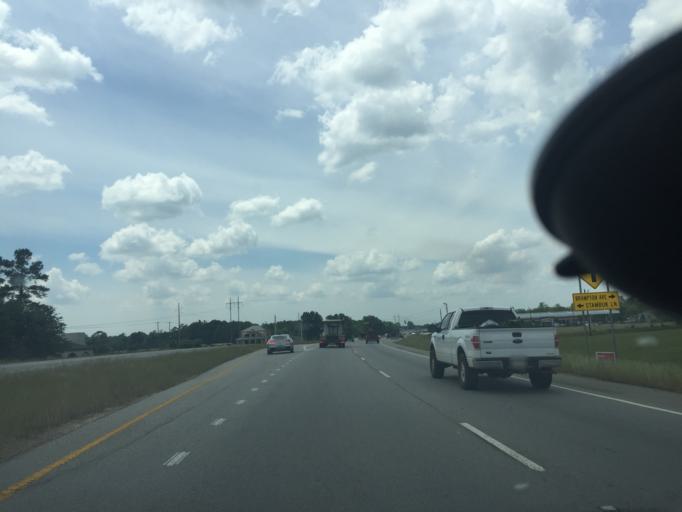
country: US
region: Georgia
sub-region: Bulloch County
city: Statesboro
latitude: 32.4061
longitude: -81.7672
